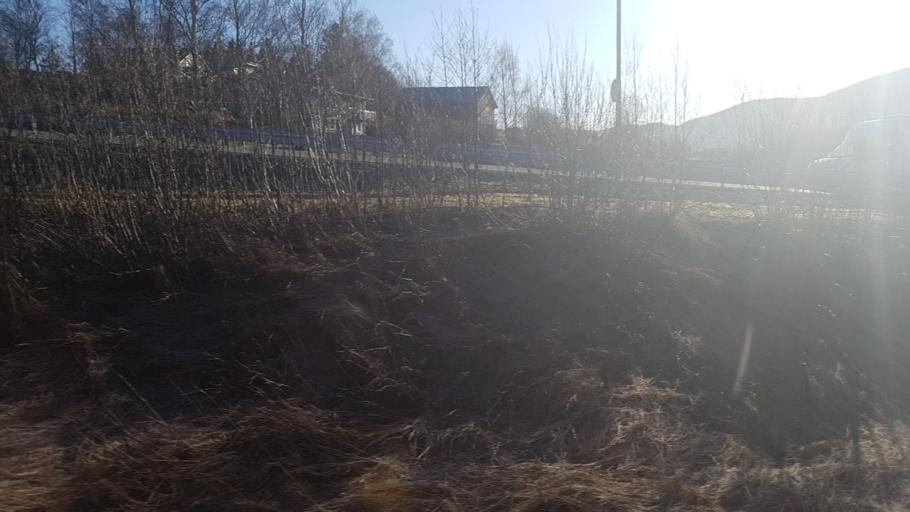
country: NO
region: Nord-Trondelag
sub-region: Levanger
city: Skogn
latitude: 63.6330
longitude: 11.0682
